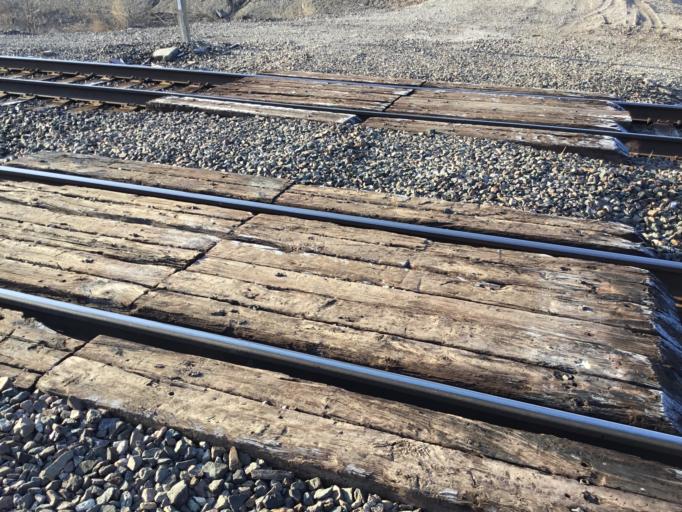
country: US
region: Kansas
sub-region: Lyon County
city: Emporia
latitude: 38.4057
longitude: -96.3366
